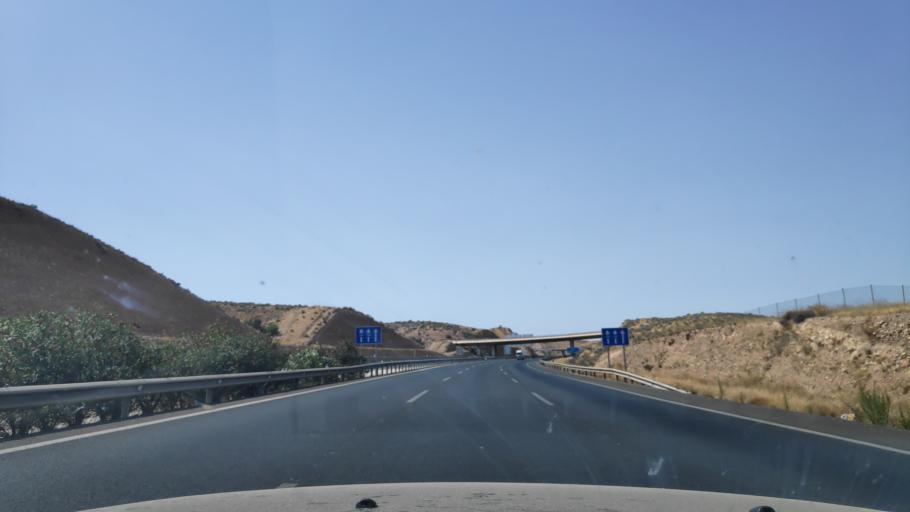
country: ES
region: Murcia
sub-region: Murcia
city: Molina de Segura
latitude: 38.0347
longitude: -1.1597
